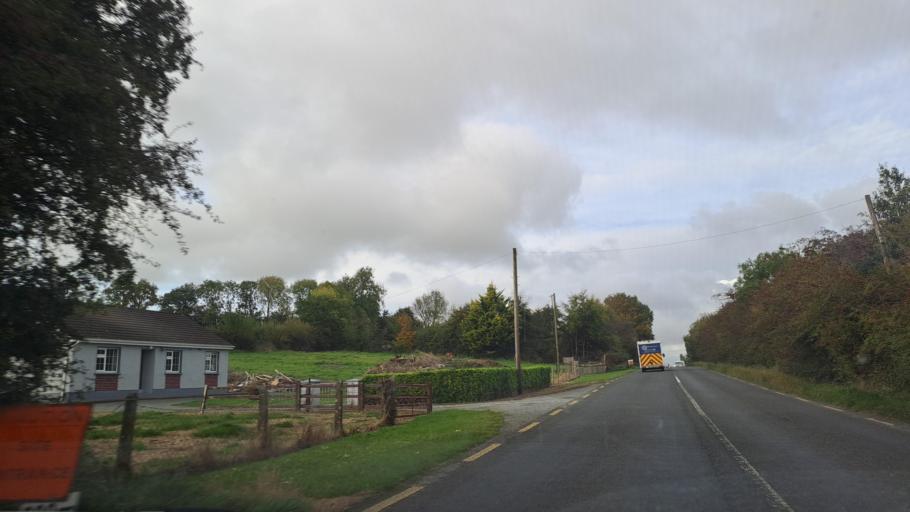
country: IE
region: Ulster
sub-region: An Cabhan
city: Kingscourt
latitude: 53.7997
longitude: -6.7381
